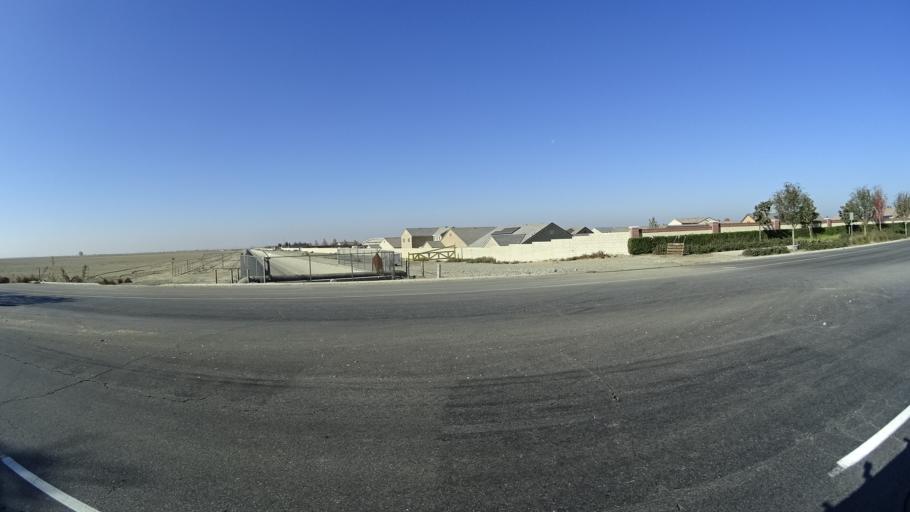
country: US
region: California
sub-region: Kern County
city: Rosedale
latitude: 35.3377
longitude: -119.1455
